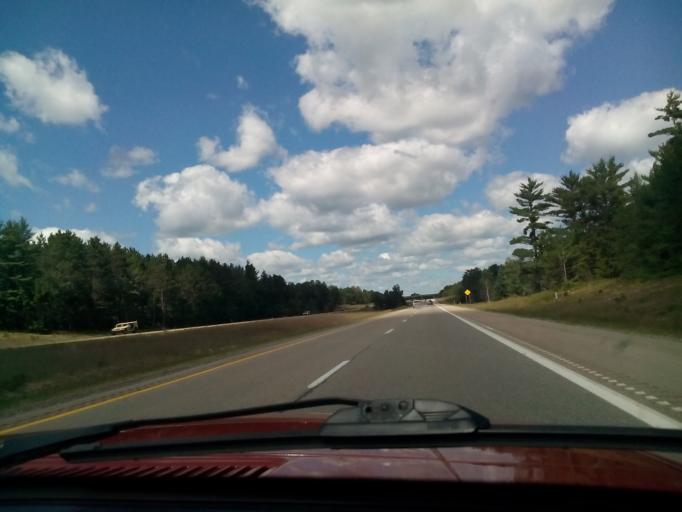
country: US
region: Michigan
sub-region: Crawford County
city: Grayling
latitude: 44.6629
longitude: -84.6970
